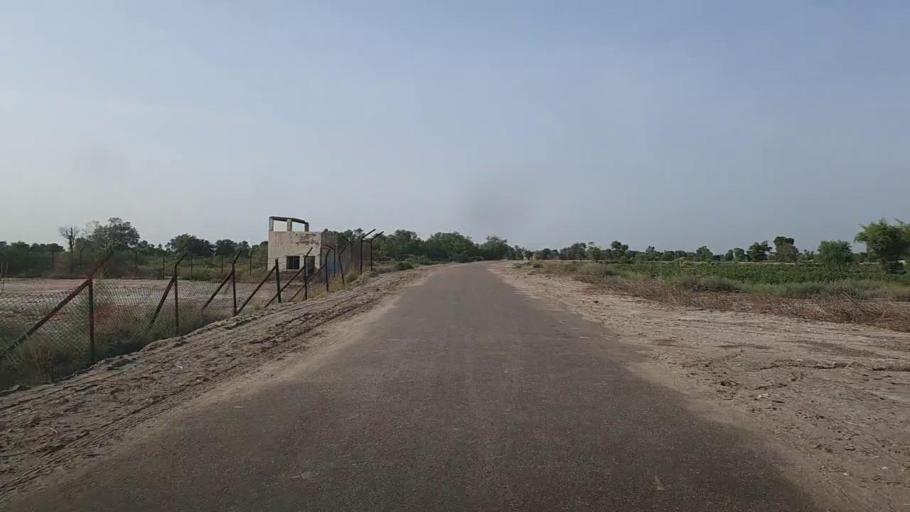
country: PK
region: Sindh
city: Ubauro
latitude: 28.0978
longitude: 69.8456
